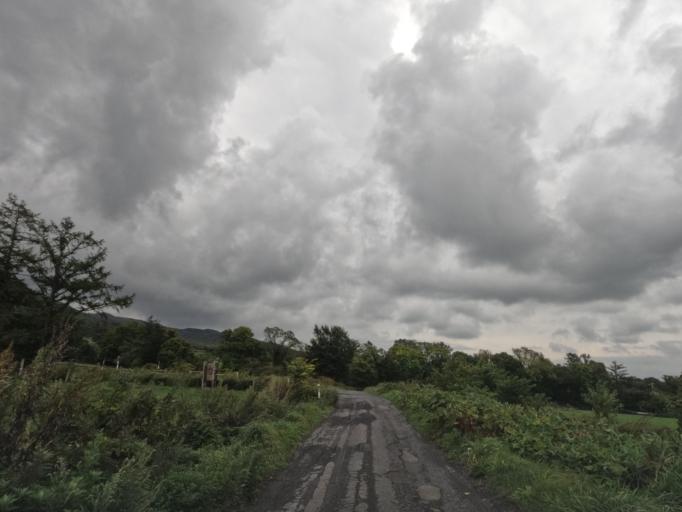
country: JP
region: Hokkaido
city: Date
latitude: 42.4941
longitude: 140.9021
